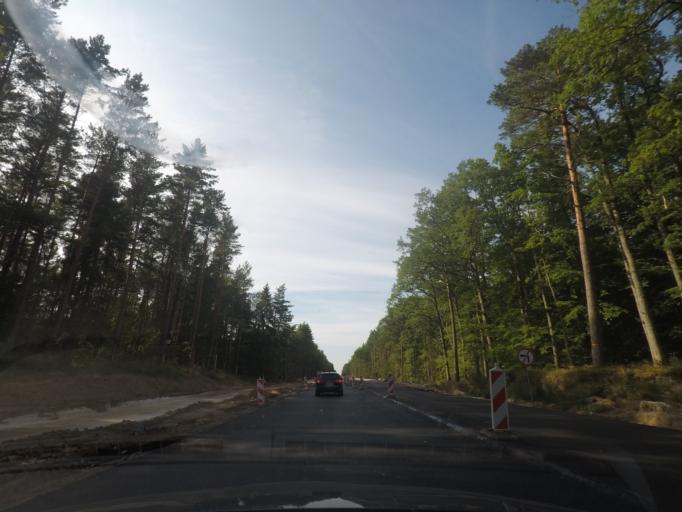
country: PL
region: Pomeranian Voivodeship
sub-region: Powiat leborski
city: Leba
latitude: 54.7008
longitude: 17.5872
